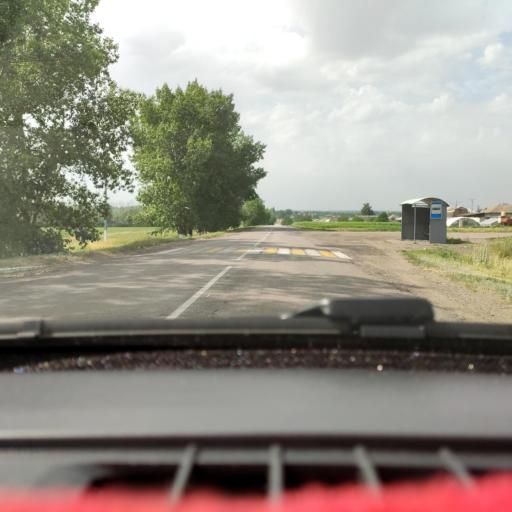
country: RU
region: Voronezj
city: Davydovka
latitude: 51.2456
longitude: 39.5435
